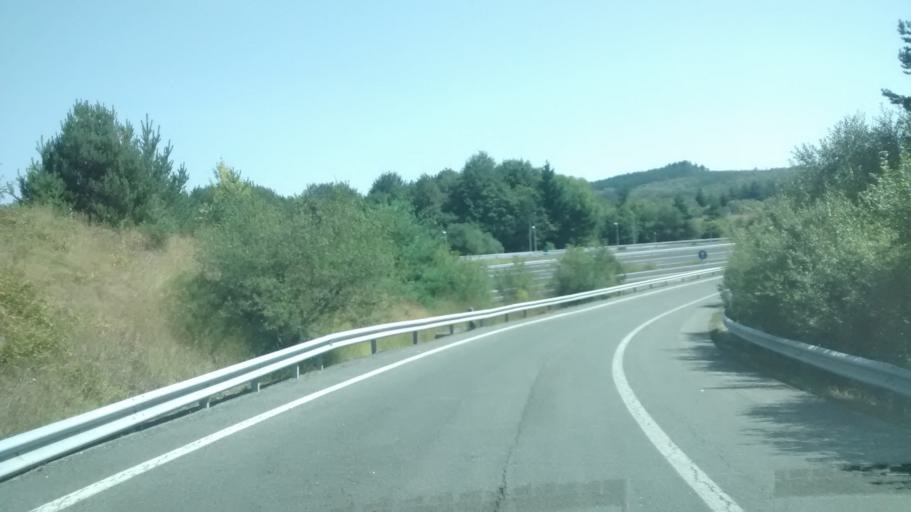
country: ES
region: Basque Country
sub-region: Provincia de Alava
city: Murguia
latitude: 42.9640
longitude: -2.8706
